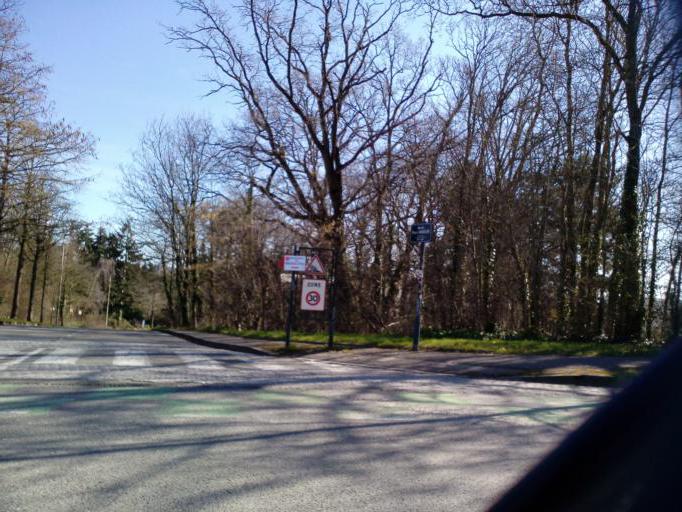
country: FR
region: Brittany
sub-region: Departement d'Ille-et-Vilaine
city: Rennes
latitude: 48.1260
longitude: -1.6418
